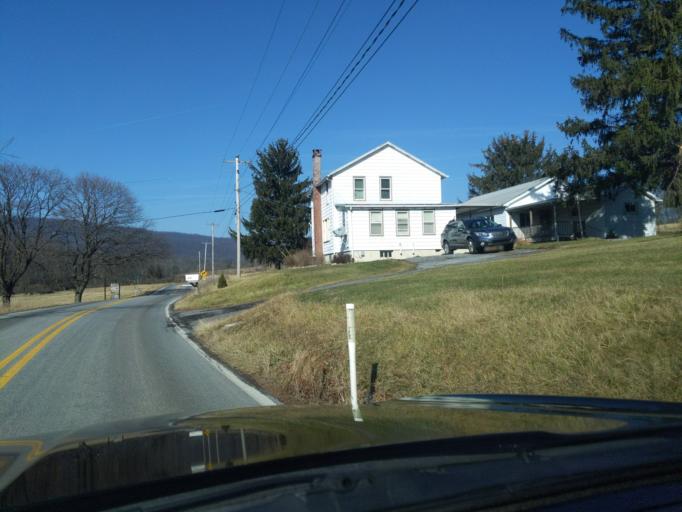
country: US
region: Pennsylvania
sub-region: Blair County
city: Tipton
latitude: 40.5831
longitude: -78.2629
